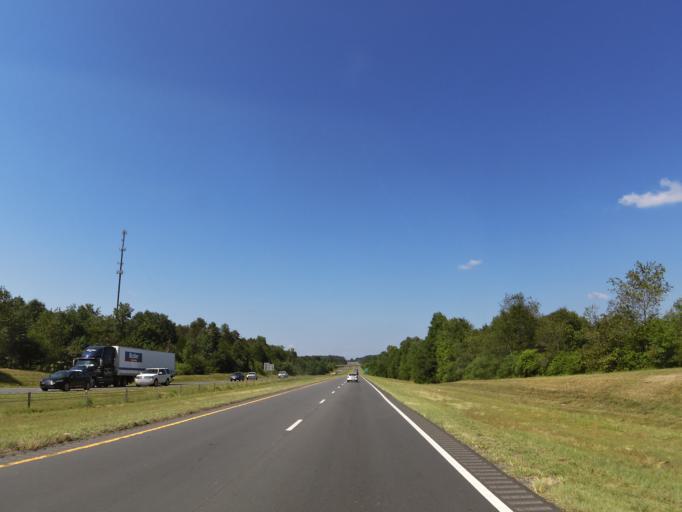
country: US
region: North Carolina
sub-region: Lincoln County
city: Lincolnton
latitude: 35.5064
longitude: -81.2239
